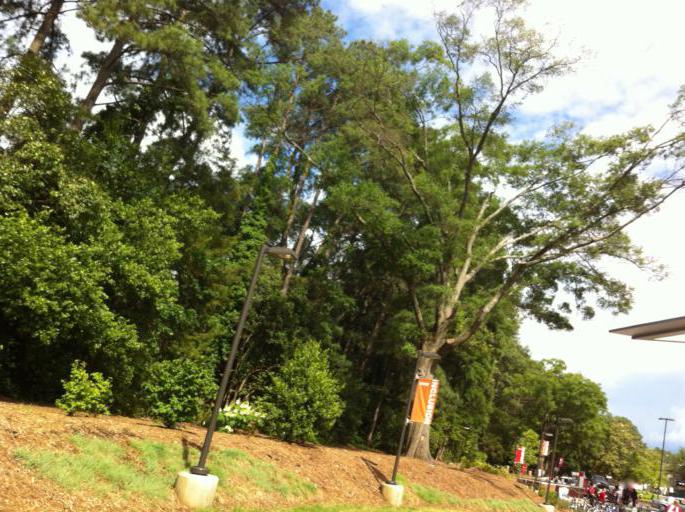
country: US
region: North Carolina
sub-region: Wake County
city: West Raleigh
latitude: 35.7847
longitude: -78.6707
